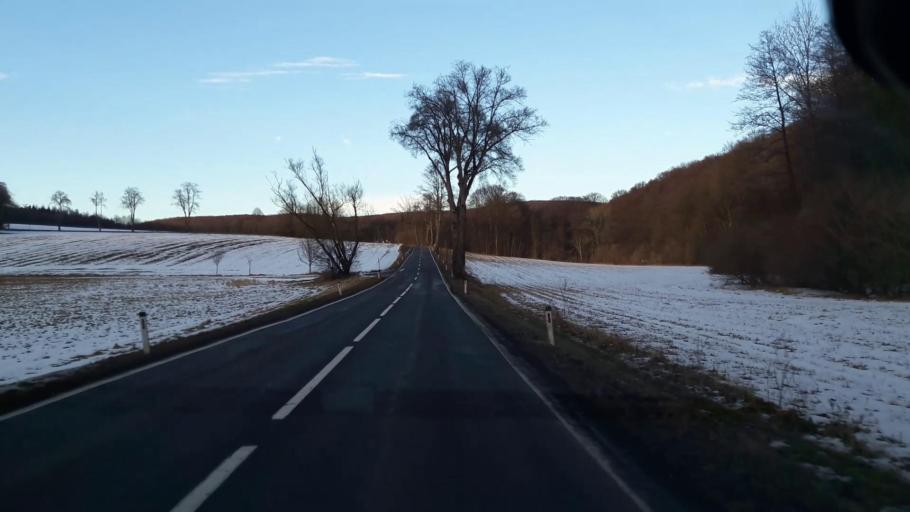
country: AT
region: Lower Austria
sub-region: Politischer Bezirk Wien-Umgebung
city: Mauerbach
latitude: 48.2624
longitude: 16.1689
